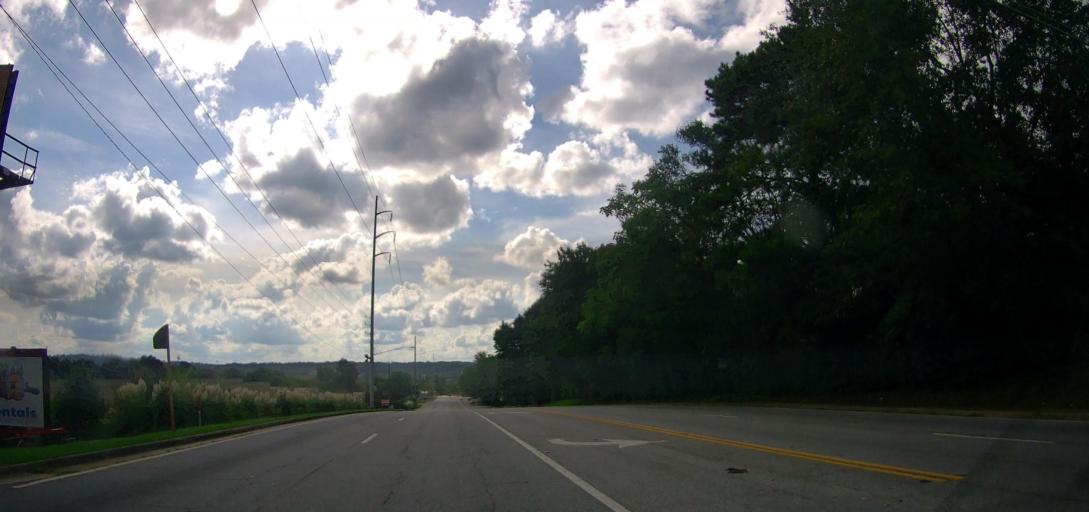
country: US
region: Alabama
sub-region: Russell County
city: Phenix City
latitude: 32.5073
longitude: -84.9840
